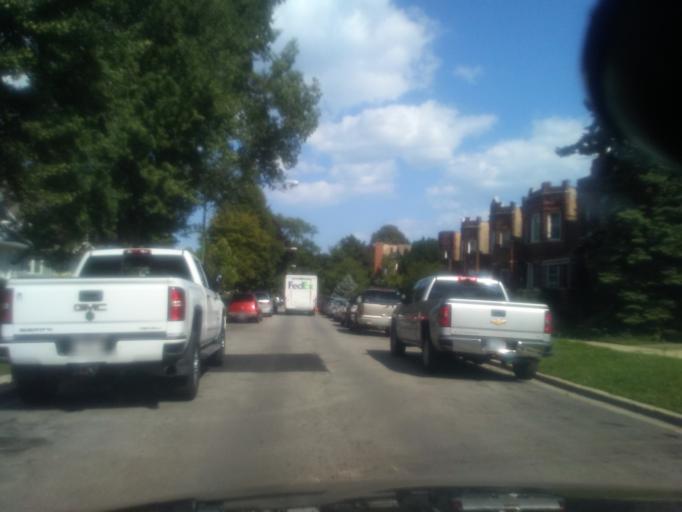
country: US
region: Illinois
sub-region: Cook County
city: Lincolnwood
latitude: 41.9589
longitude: -87.7517
